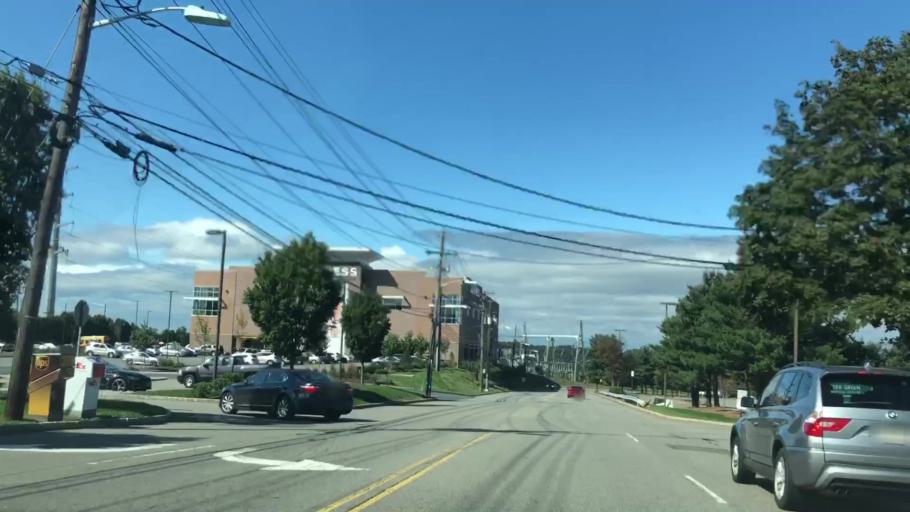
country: US
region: New Jersey
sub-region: Essex County
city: West Orange
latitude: 40.7914
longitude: -74.2554
